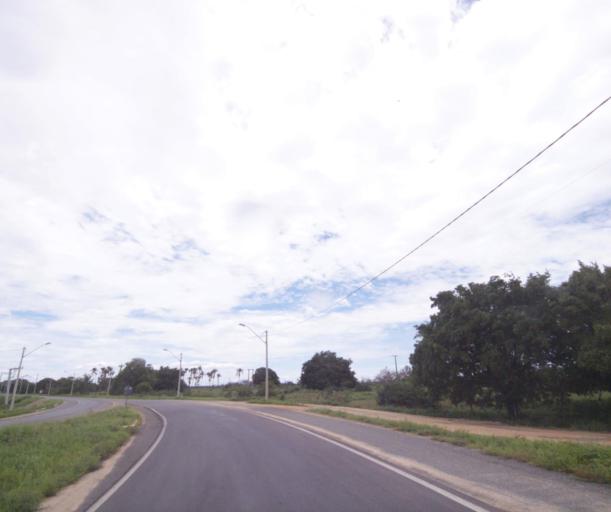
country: BR
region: Bahia
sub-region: Carinhanha
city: Carinhanha
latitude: -14.3291
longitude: -43.7668
